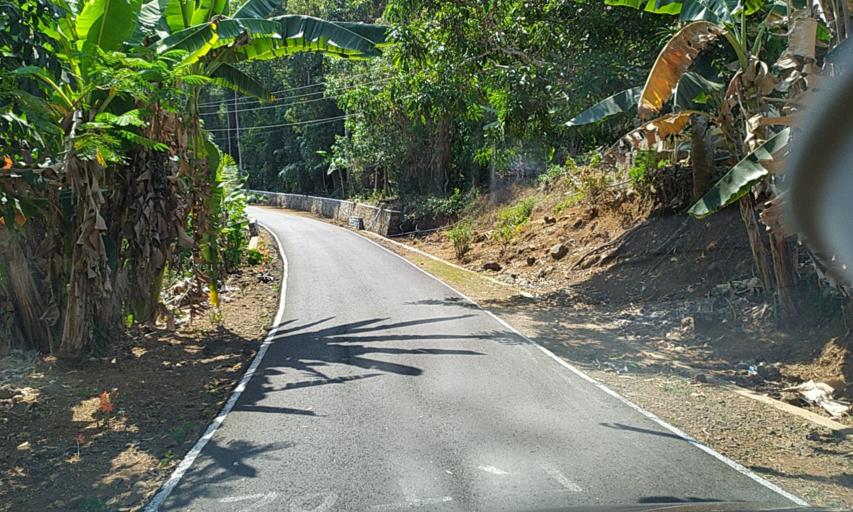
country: ID
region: Central Java
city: Cimalati
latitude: -7.3061
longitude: 108.6471
